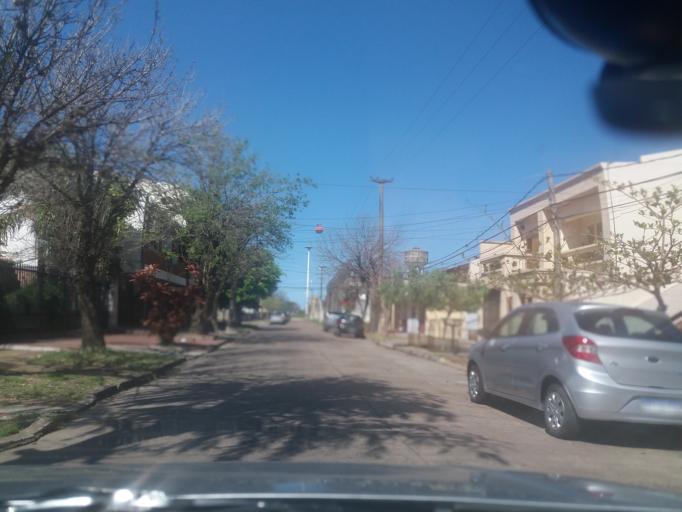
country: AR
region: Corrientes
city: Corrientes
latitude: -27.4716
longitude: -58.8497
